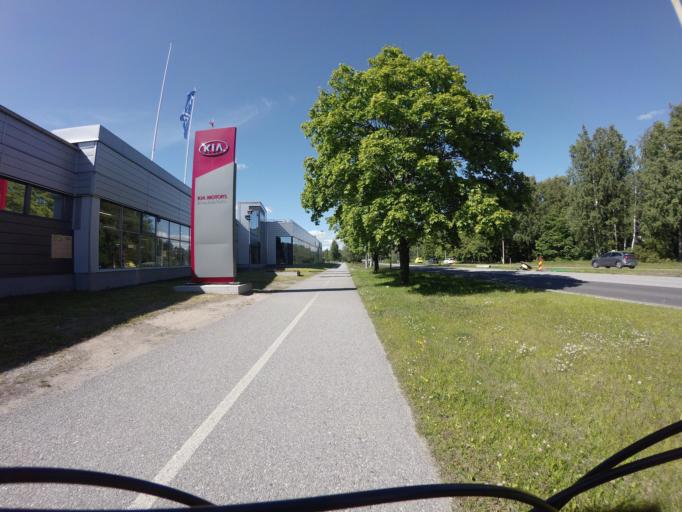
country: FI
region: Varsinais-Suomi
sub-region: Turku
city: Turku
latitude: 60.4713
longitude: 22.2652
